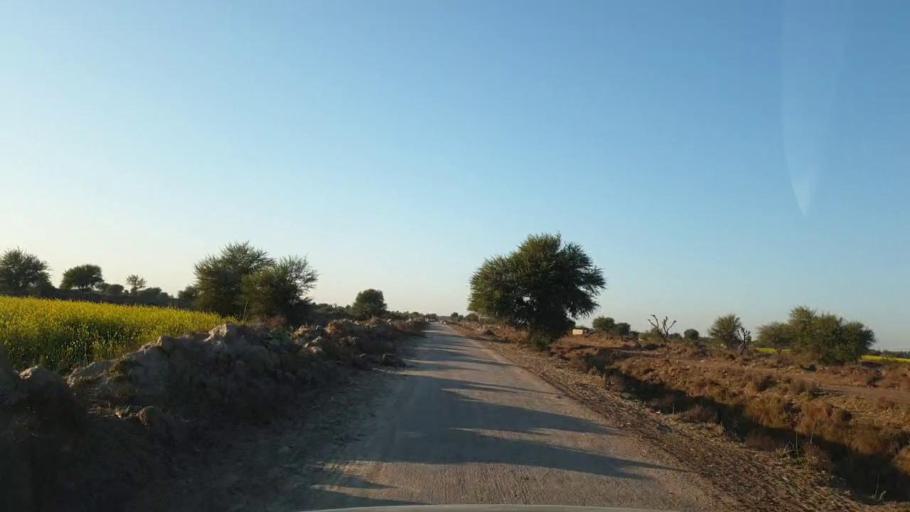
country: PK
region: Sindh
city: Jhol
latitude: 25.8855
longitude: 68.8984
